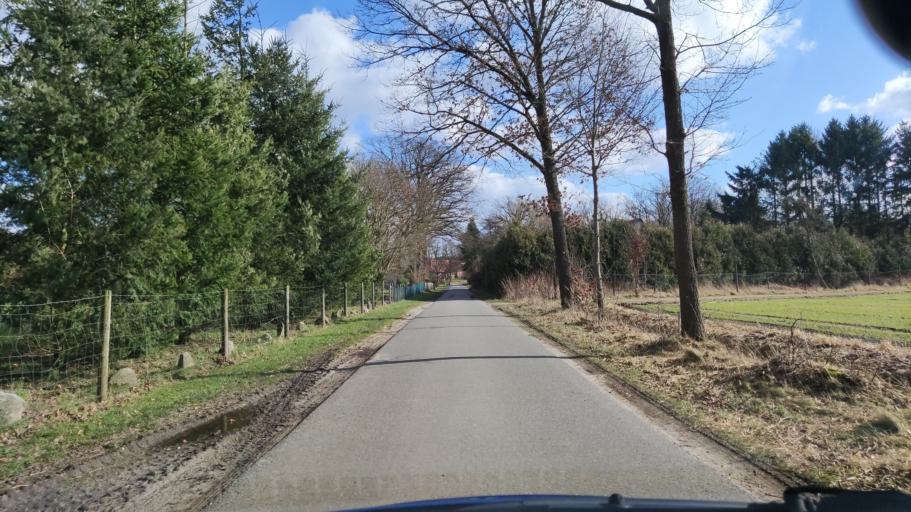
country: DE
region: Lower Saxony
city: Eldingen
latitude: 52.7036
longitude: 10.3412
